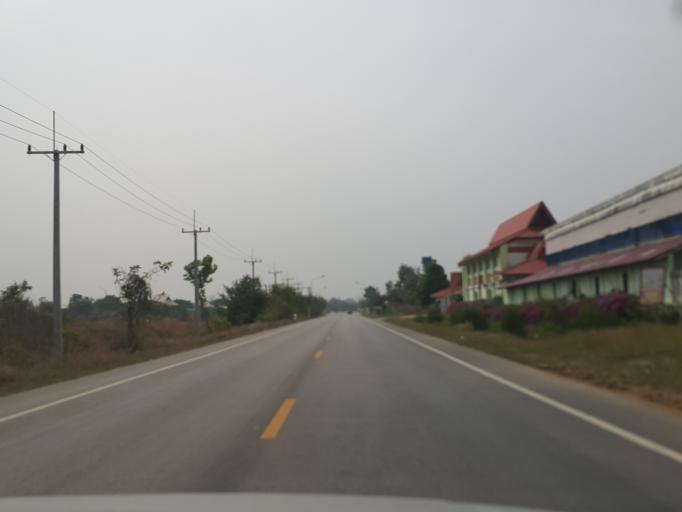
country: TH
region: Lampang
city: Ko Kha
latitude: 18.2111
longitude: 99.3918
